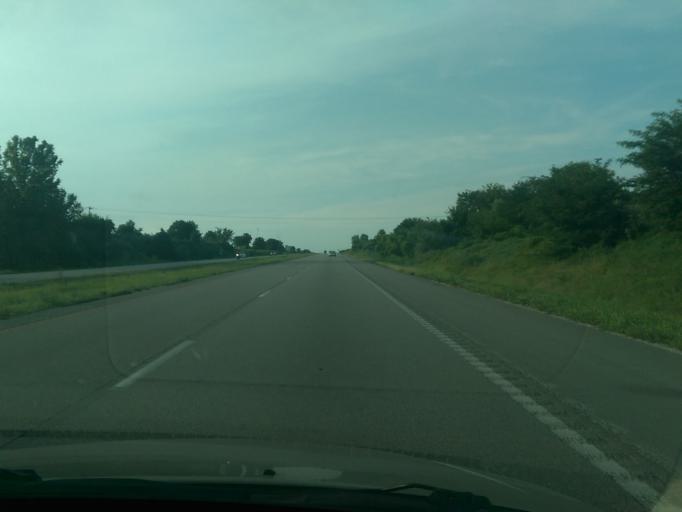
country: US
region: Missouri
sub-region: Platte County
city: Platte City
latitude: 39.3957
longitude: -94.7894
